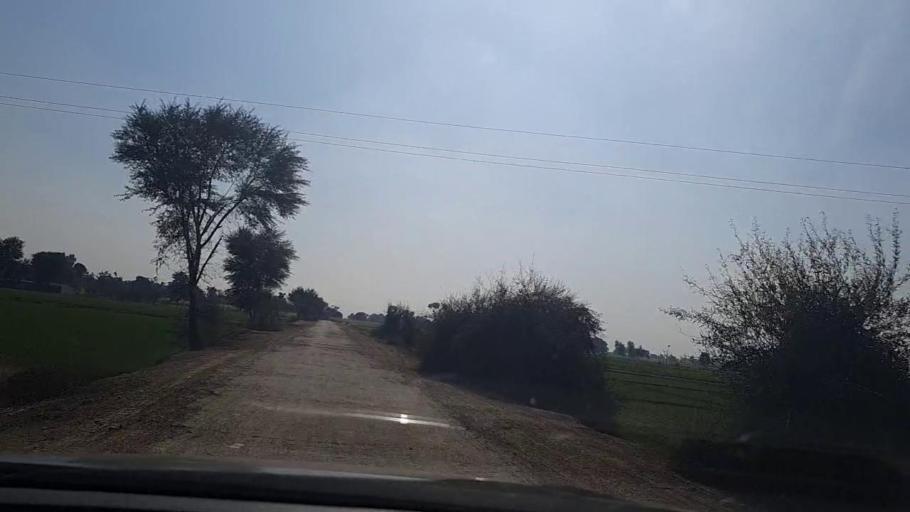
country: PK
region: Sindh
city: Daulatpur
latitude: 26.2877
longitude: 68.0678
